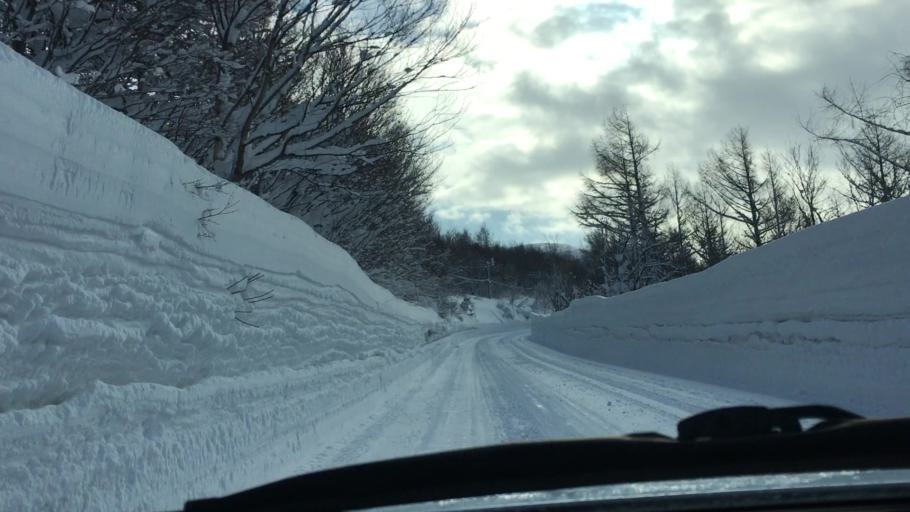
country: JP
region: Aomori
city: Aomori Shi
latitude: 40.6487
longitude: 140.7808
